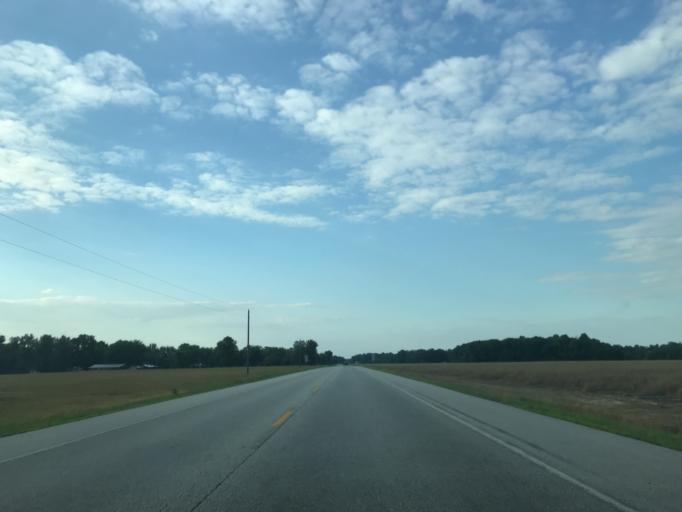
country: US
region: Maryland
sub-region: Caroline County
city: Federalsburg
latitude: 38.7636
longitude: -75.7891
